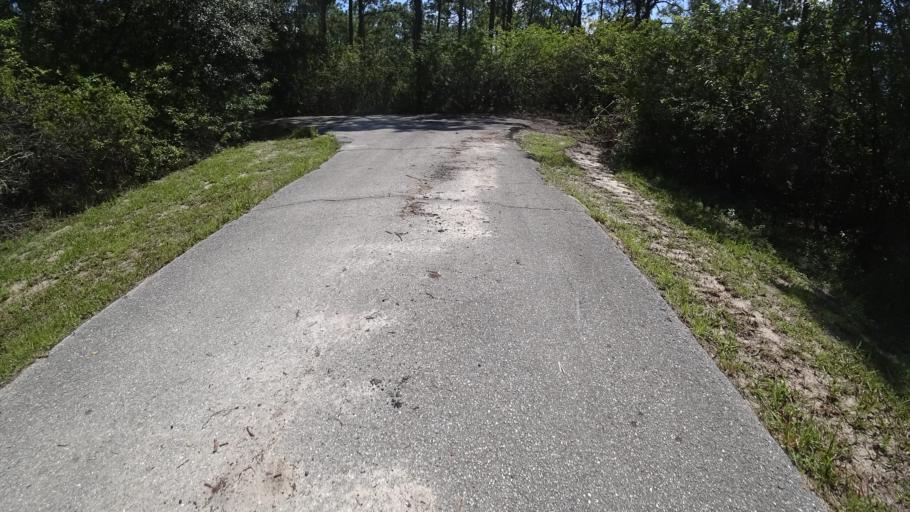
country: US
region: Florida
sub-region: Sarasota County
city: The Meadows
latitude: 27.4258
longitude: -82.3230
